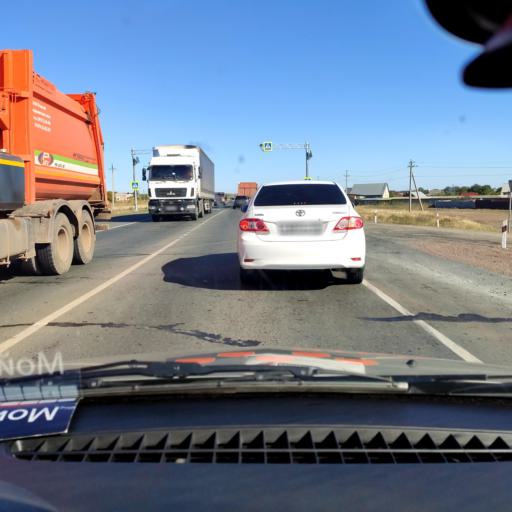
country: RU
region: Orenburg
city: Nezhinka
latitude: 51.7771
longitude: 55.5646
